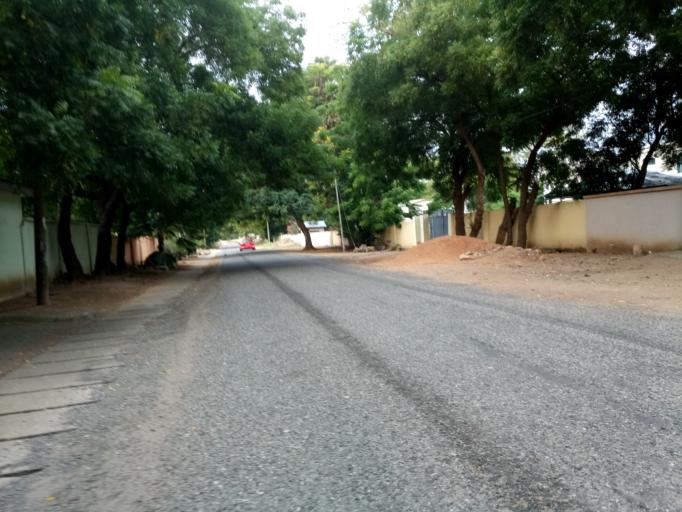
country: GH
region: Greater Accra
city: Accra
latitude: 5.5620
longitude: -0.1900
